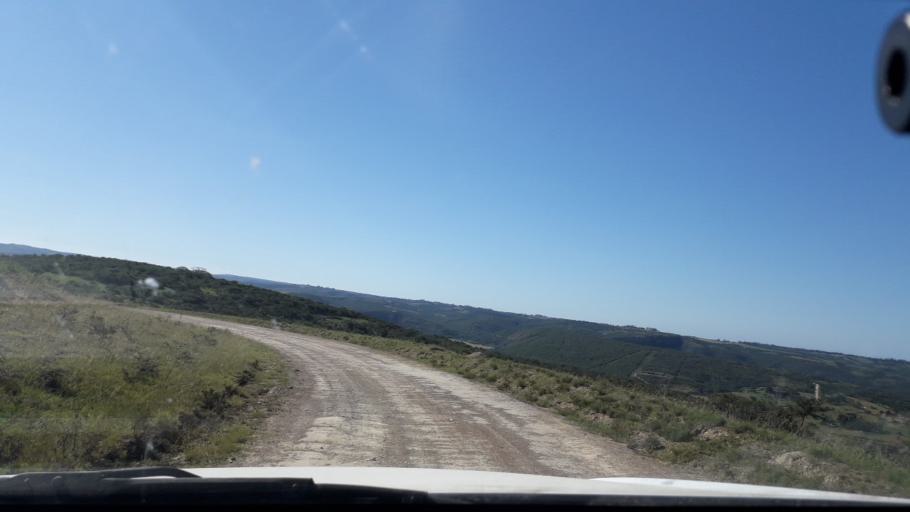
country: ZA
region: Eastern Cape
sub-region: Amathole District Municipality
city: Komga
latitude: -32.7839
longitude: 27.9564
